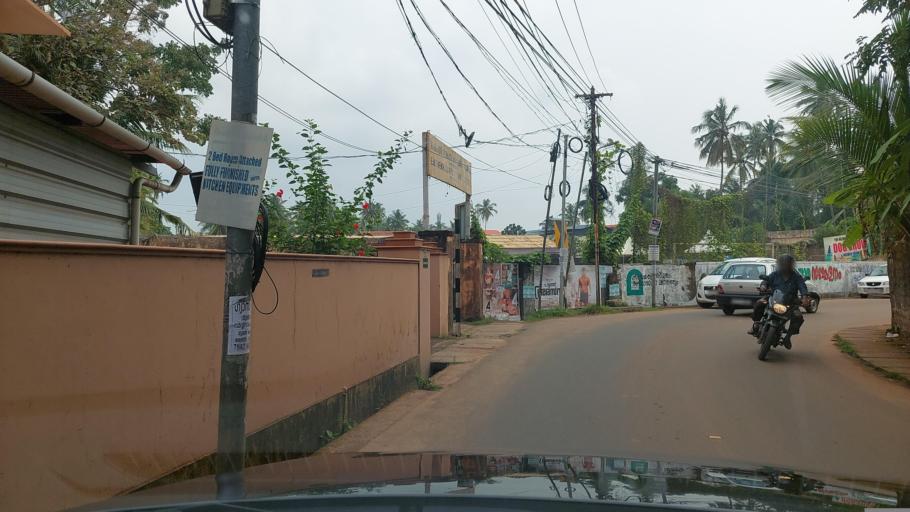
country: IN
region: Kerala
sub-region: Kozhikode
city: Kozhikode
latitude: 11.2492
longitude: 75.7887
